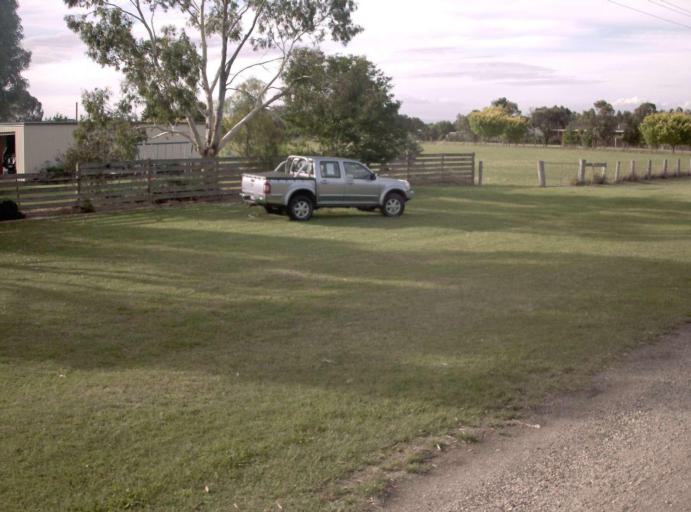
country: AU
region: Victoria
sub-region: Wellington
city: Sale
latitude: -37.9525
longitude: 146.9877
